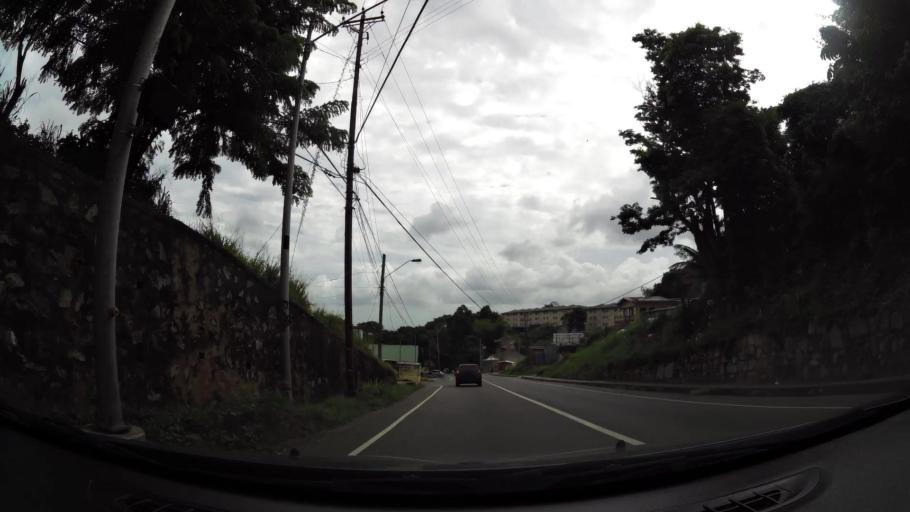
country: TT
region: San Juan/Laventille
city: Laventille
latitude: 10.6688
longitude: -61.4886
